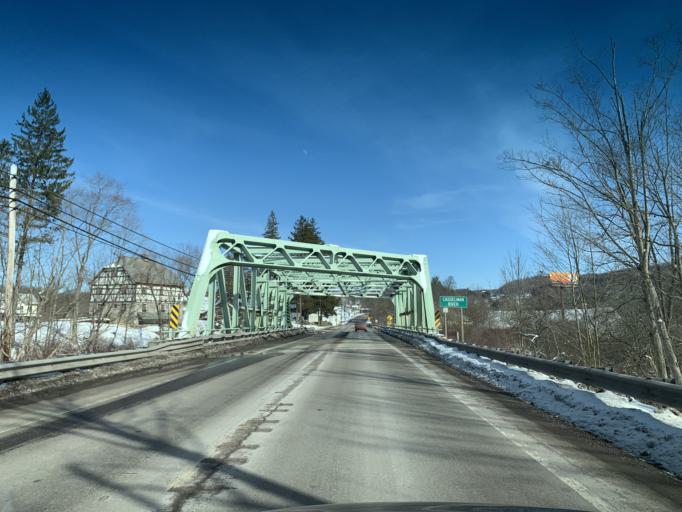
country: US
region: Pennsylvania
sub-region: Somerset County
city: Meyersdale
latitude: 39.6958
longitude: -79.1429
